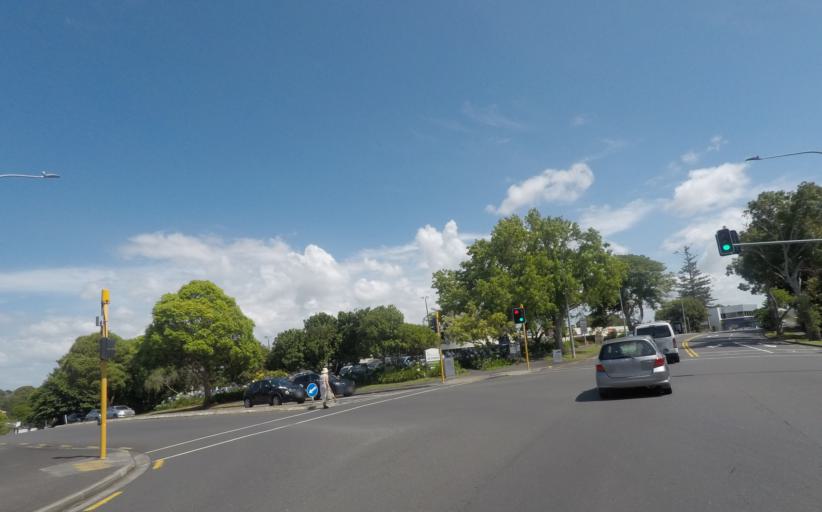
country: NZ
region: Auckland
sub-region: Auckland
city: Tamaki
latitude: -36.8748
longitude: 174.8282
